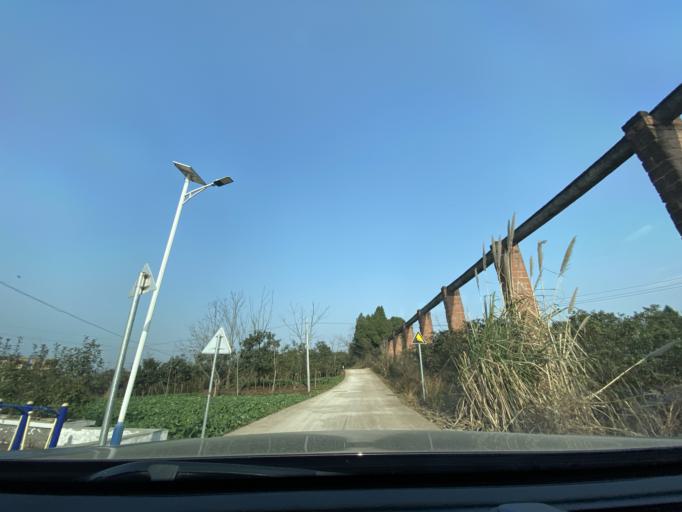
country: CN
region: Sichuan
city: Wenlin
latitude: 30.2497
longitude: 104.2500
